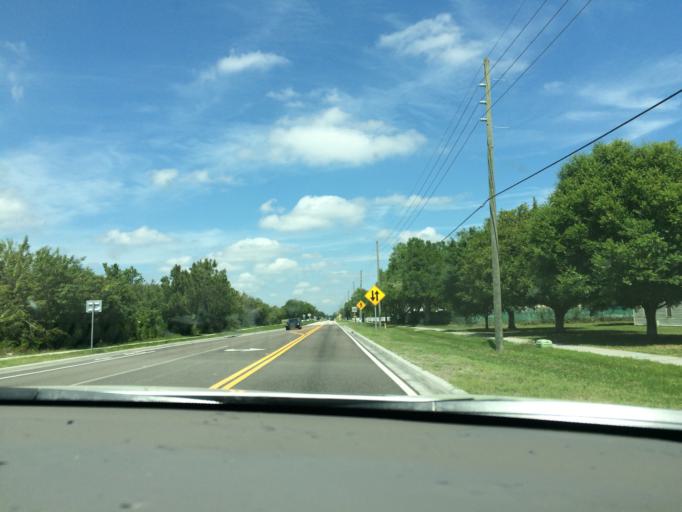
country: US
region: Florida
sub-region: Manatee County
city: Ellenton
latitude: 27.4897
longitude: -82.4337
